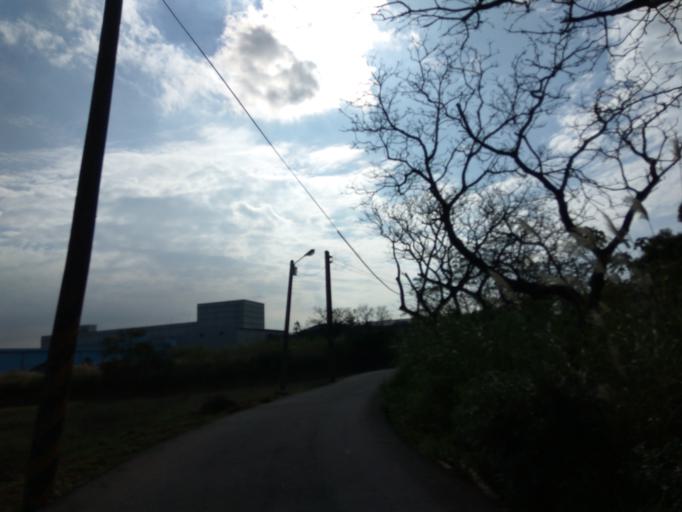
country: TW
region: Taiwan
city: Taoyuan City
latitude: 25.0517
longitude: 121.1784
